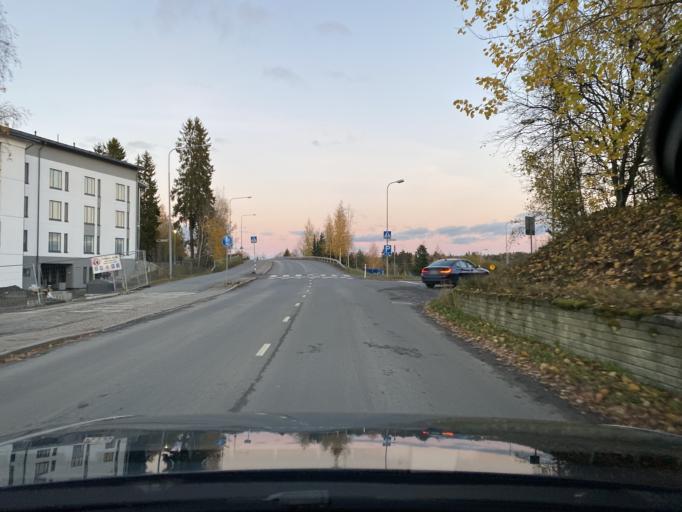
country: FI
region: Pirkanmaa
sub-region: Tampere
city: Lempaeaelae
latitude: 61.3264
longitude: 23.7556
